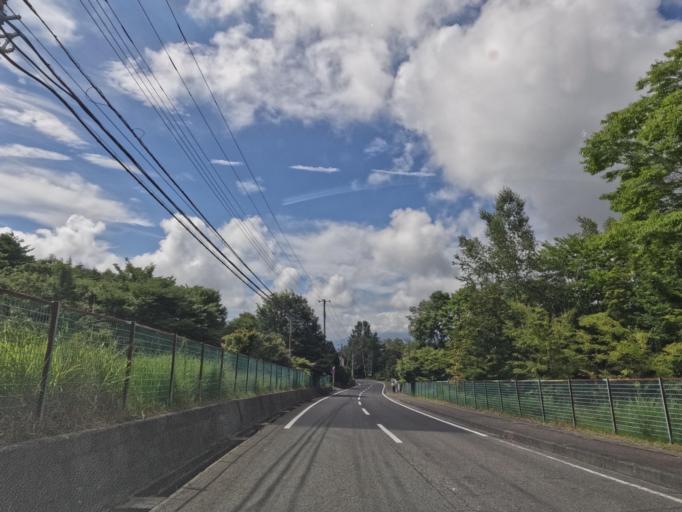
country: JP
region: Yamanashi
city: Nirasaki
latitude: 35.8922
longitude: 138.4105
